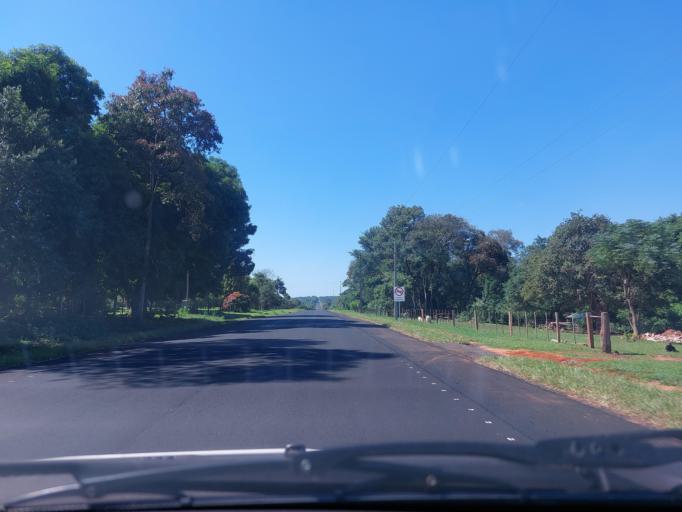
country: PY
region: San Pedro
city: Guayaybi
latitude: -24.5504
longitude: -56.4953
